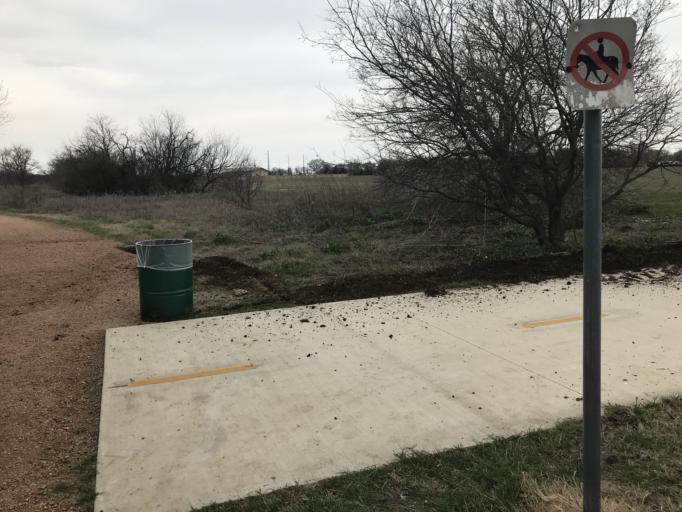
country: US
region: Texas
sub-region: Denton County
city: Denton
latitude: 33.2448
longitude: -97.1465
